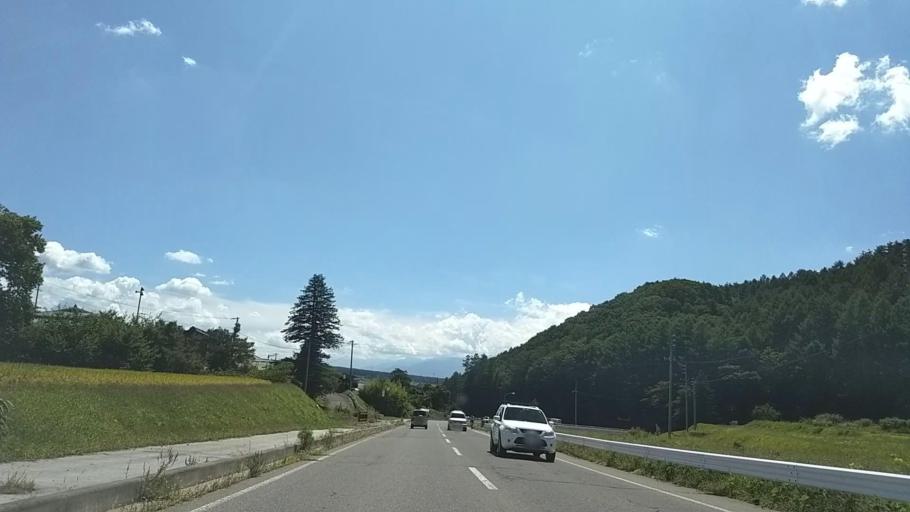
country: JP
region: Nagano
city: Chino
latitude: 36.0547
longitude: 138.2244
